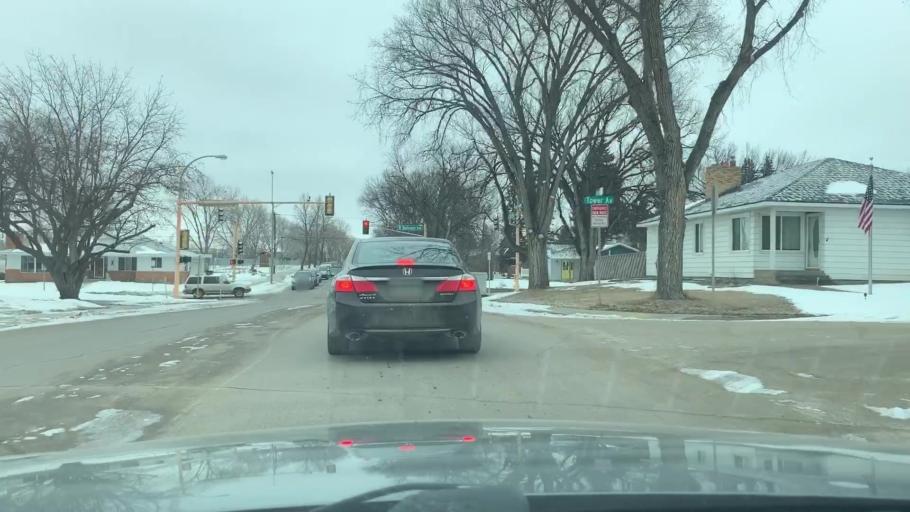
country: US
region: North Dakota
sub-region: Burleigh County
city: Bismarck
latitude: 46.8162
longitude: -100.7942
